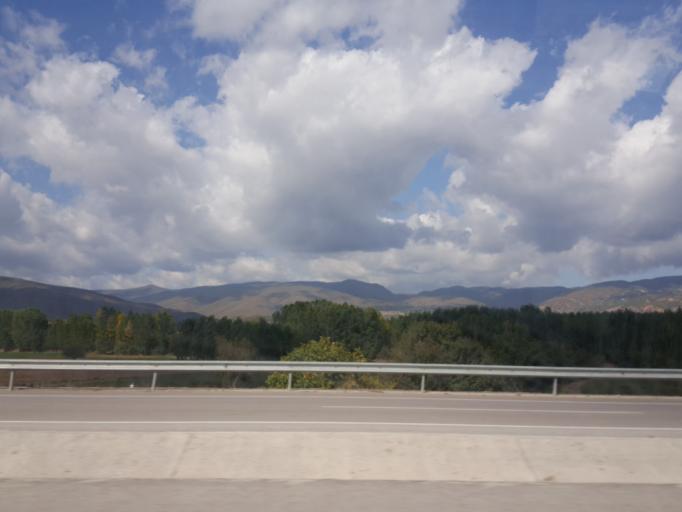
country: TR
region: Tokat
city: Gokdere
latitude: 40.4231
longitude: 36.7212
